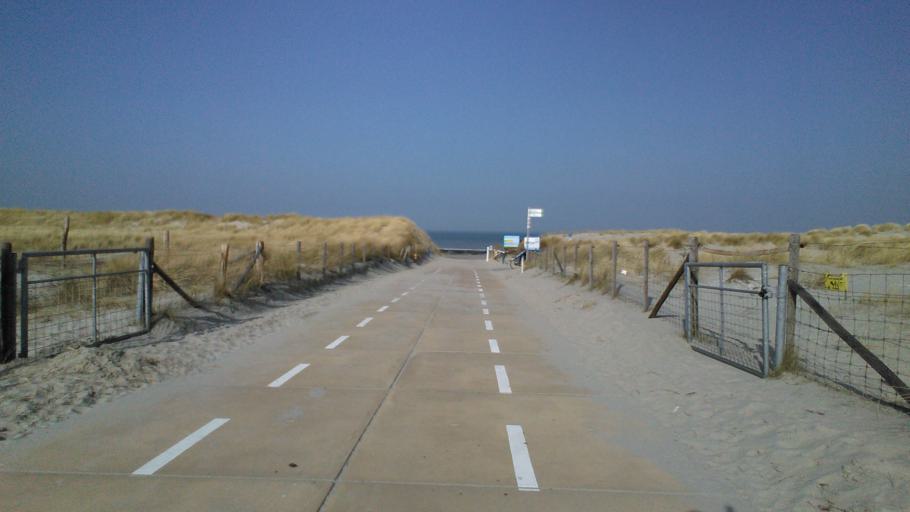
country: NL
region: South Holland
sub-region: Gemeente Westland
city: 's-Gravenzande
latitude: 52.0170
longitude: 4.1488
